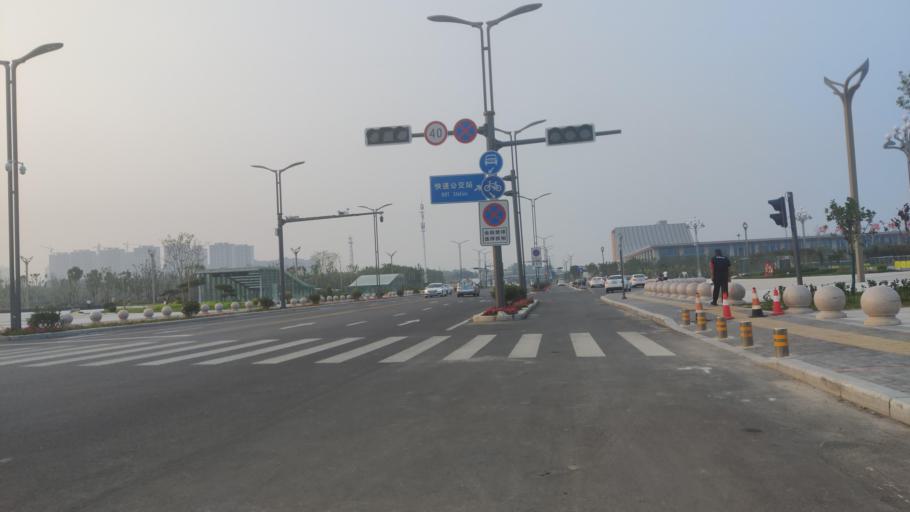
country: CN
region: Henan Sheng
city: Zhongyuanlu
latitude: 35.7642
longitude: 115.1405
